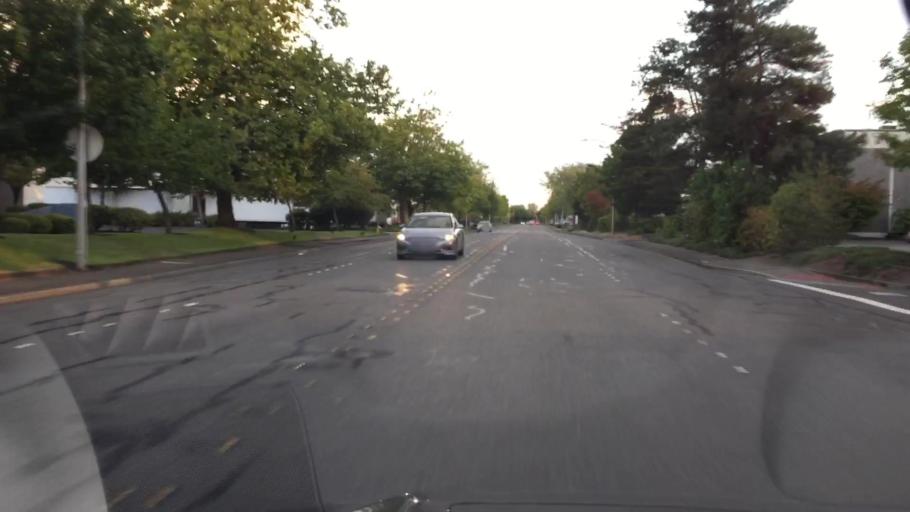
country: US
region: Washington
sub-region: King County
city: Tukwila
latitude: 47.4474
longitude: -122.2545
